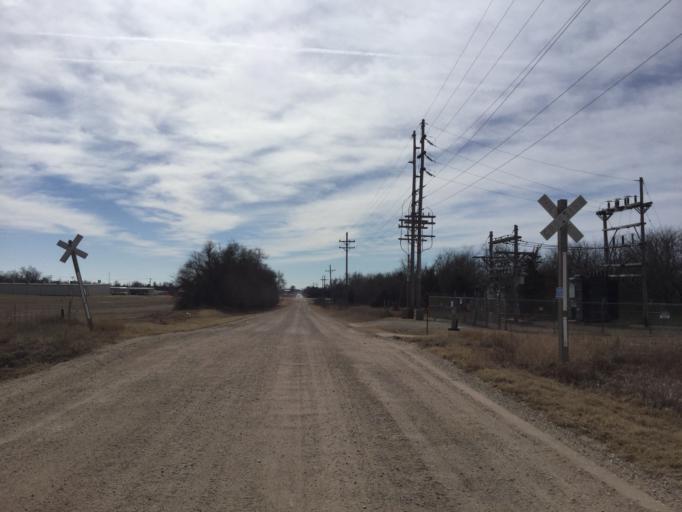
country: US
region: Kansas
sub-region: Rice County
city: Lyons
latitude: 38.3515
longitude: -98.2203
